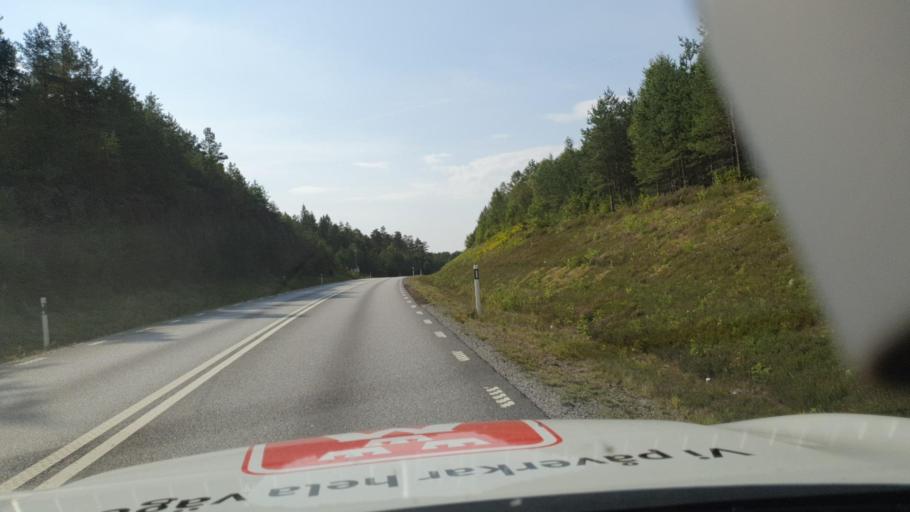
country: SE
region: Vaestra Goetaland
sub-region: Tanums Kommun
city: Tanumshede
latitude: 58.8060
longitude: 11.5987
